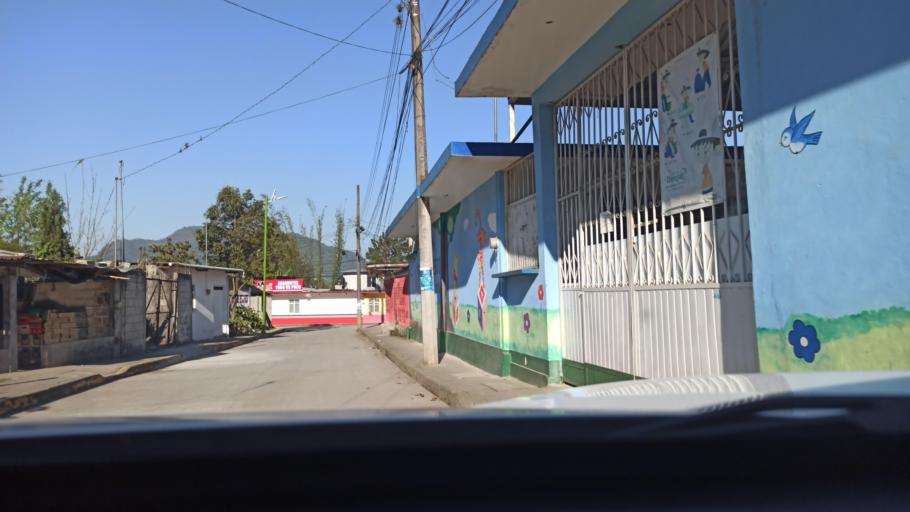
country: MX
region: Veracruz
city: Atzacan
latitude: 18.9073
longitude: -97.0875
